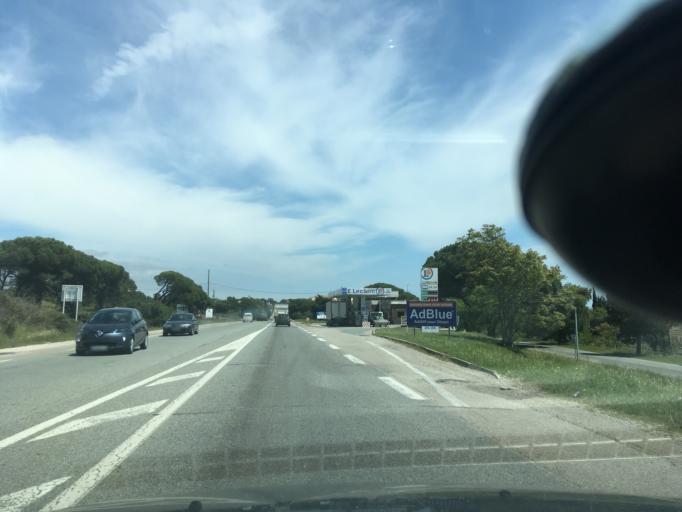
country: FR
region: Provence-Alpes-Cote d'Azur
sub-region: Departement du Var
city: Puget-sur-Argens
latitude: 43.4588
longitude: 6.6701
